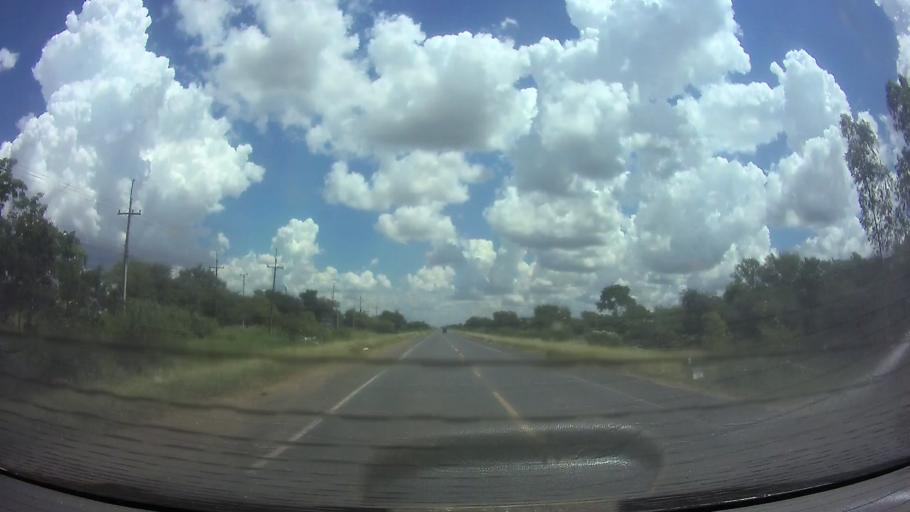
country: PY
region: Central
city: Colonia Mariano Roque Alonso
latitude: -25.1814
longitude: -57.5889
